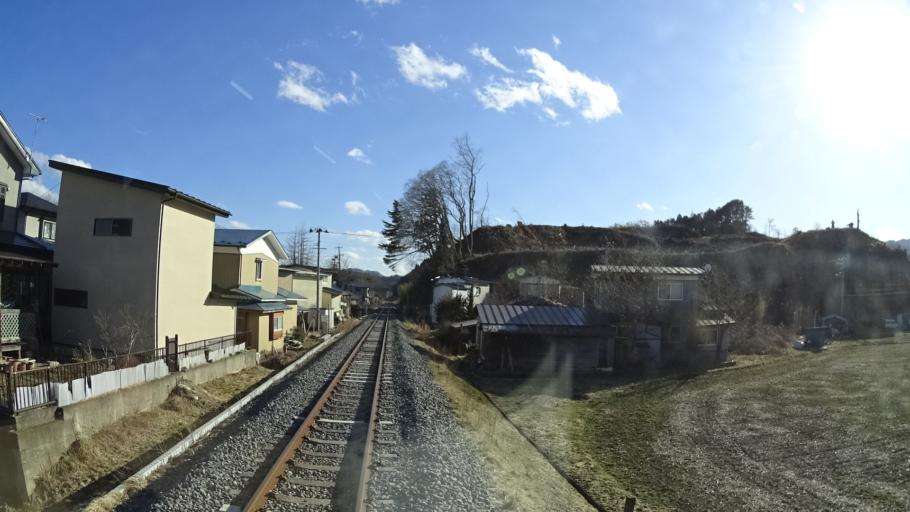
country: JP
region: Iwate
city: Miyako
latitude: 39.5747
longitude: 141.9340
